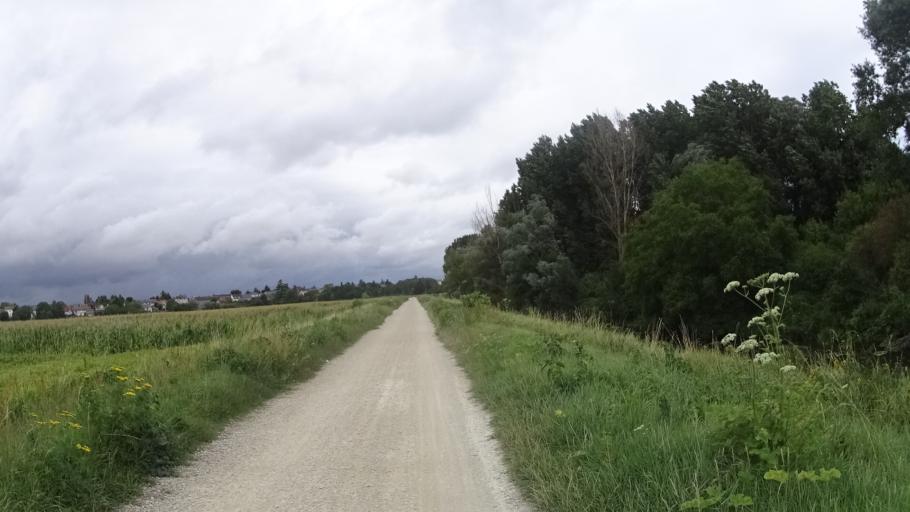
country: FR
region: Centre
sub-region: Departement du Loiret
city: Baule
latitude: 47.8077
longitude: 1.6833
